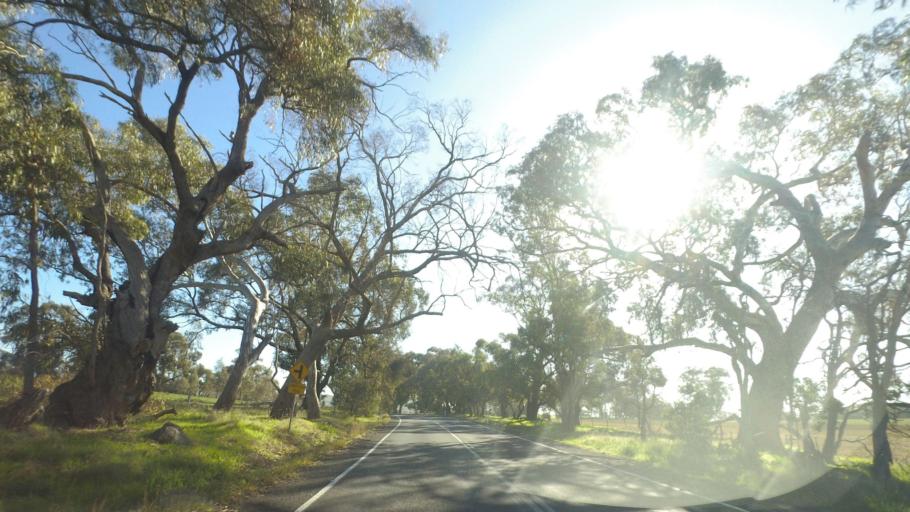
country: AU
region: Victoria
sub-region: Mount Alexander
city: Castlemaine
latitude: -36.9543
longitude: 144.3447
